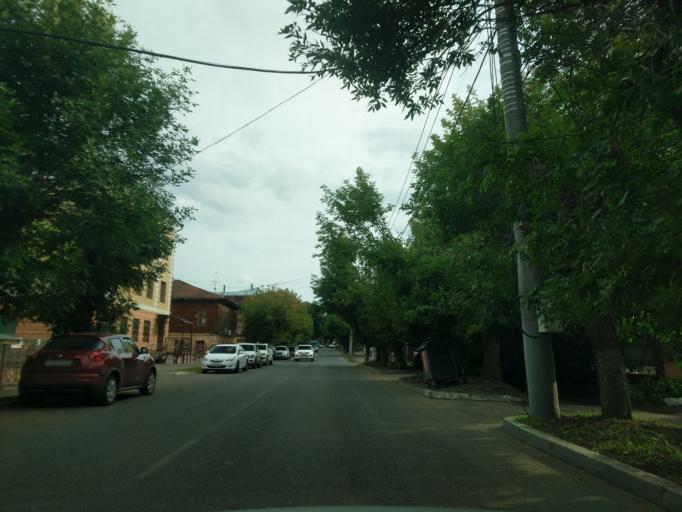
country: RU
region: Kirov
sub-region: Kirovo-Chepetskiy Rayon
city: Kirov
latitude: 58.5984
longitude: 49.6846
